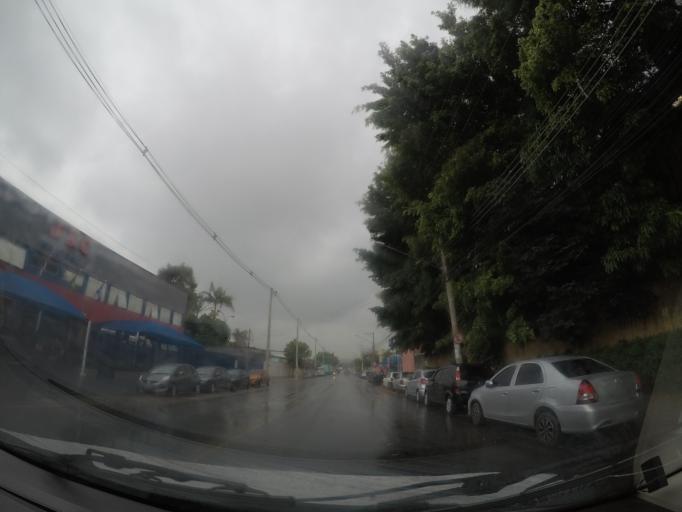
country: BR
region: Sao Paulo
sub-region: Guarulhos
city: Guarulhos
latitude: -23.4365
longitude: -46.5024
